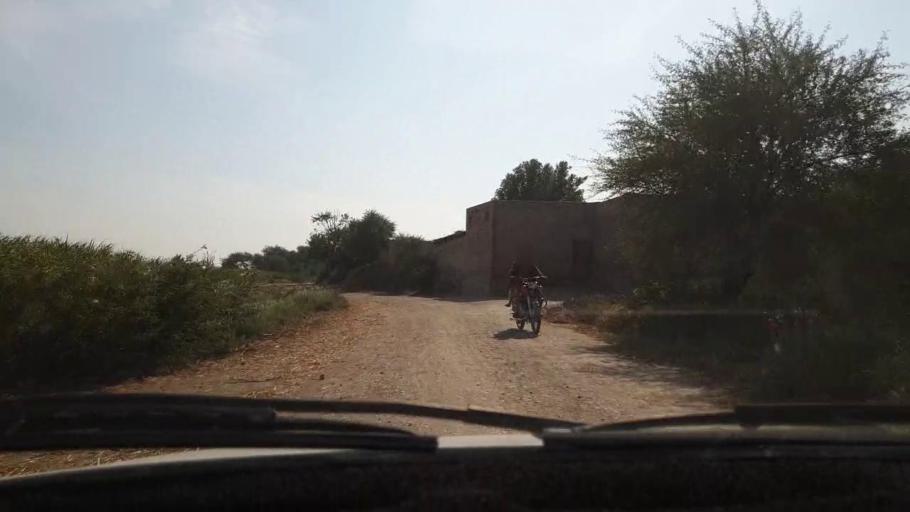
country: PK
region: Sindh
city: Bulri
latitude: 24.9438
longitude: 68.4334
